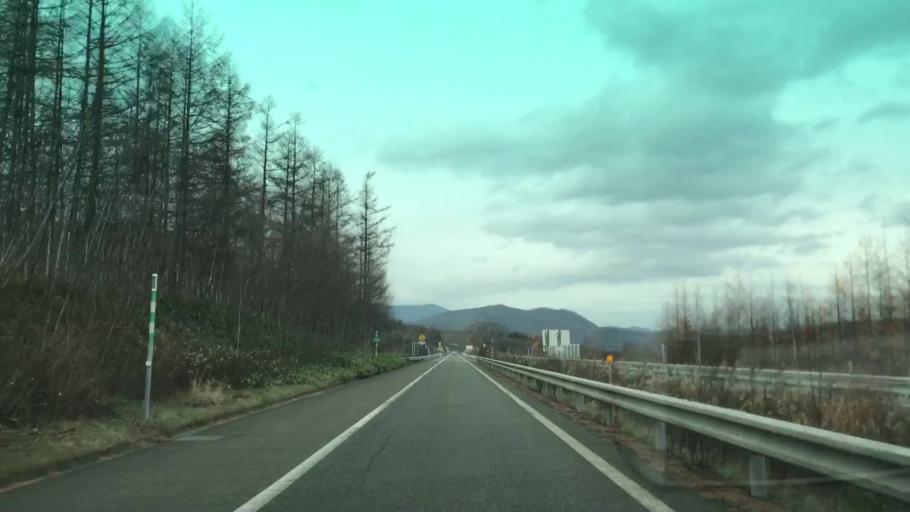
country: JP
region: Hokkaido
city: Otofuke
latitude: 42.9992
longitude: 142.8512
